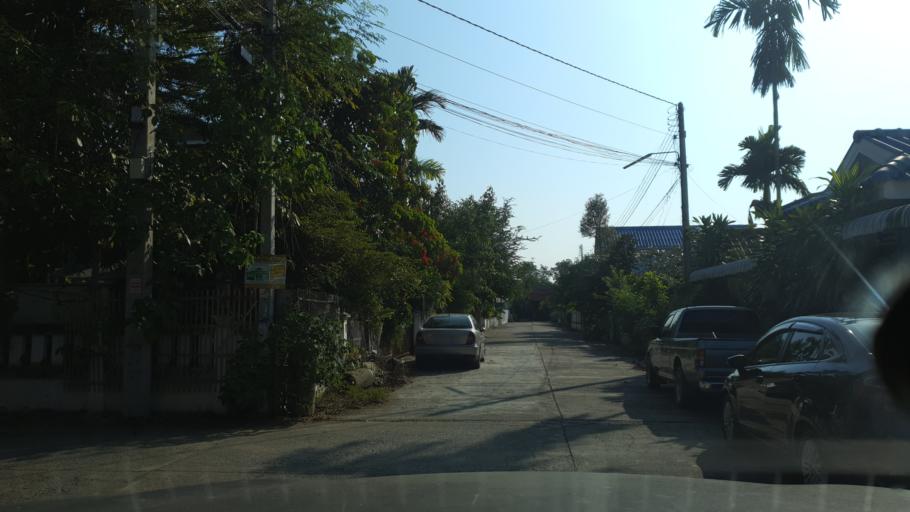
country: TH
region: Chiang Mai
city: Saraphi
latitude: 18.7163
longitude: 98.9954
